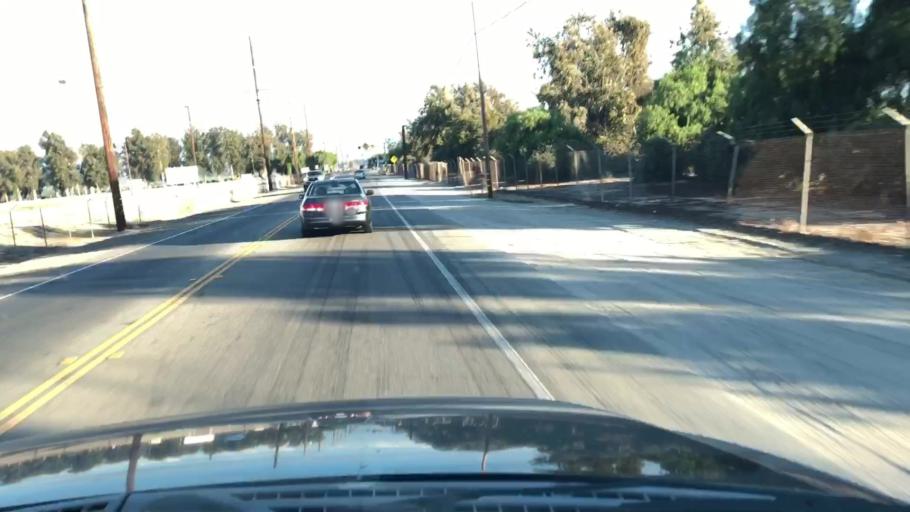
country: US
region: California
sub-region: Ventura County
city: Saticoy
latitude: 34.2702
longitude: -119.1298
